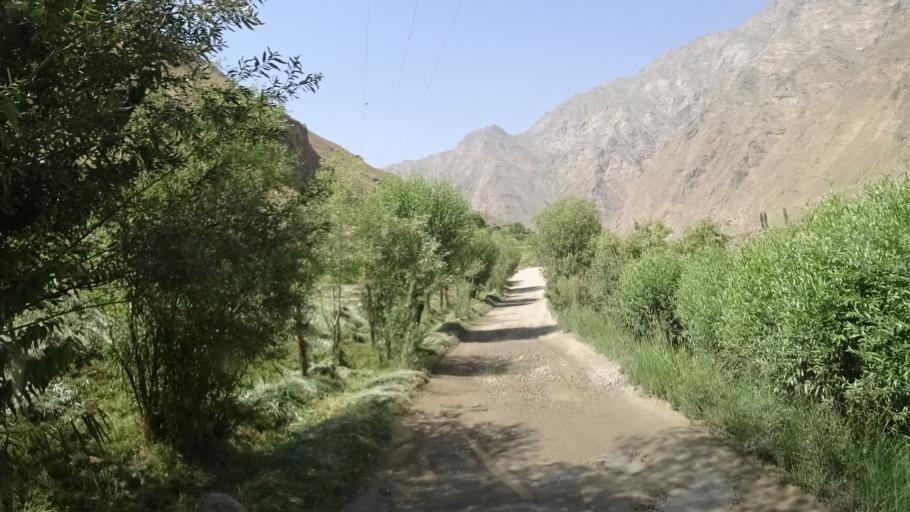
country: TJ
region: Gorno-Badakhshan
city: Khorugh
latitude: 37.1842
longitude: 71.4619
